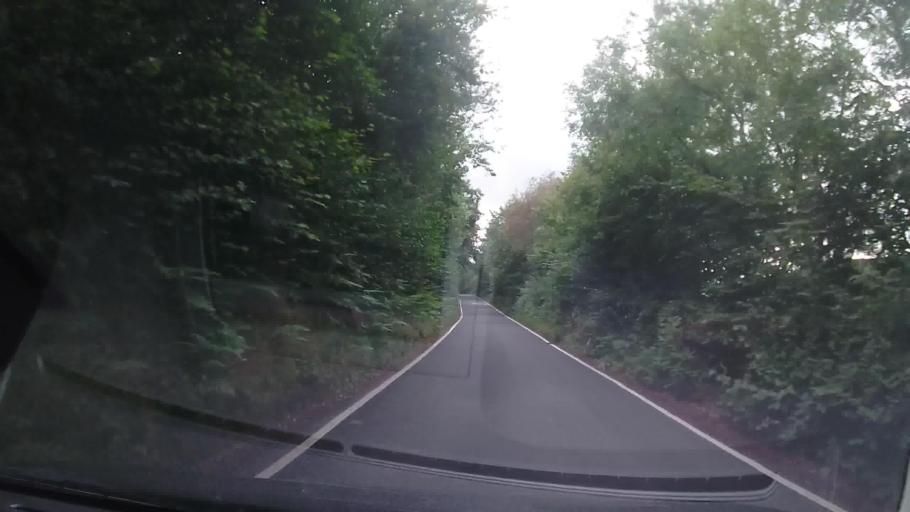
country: GB
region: England
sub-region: Shropshire
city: Norbury
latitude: 52.5955
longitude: -2.9457
